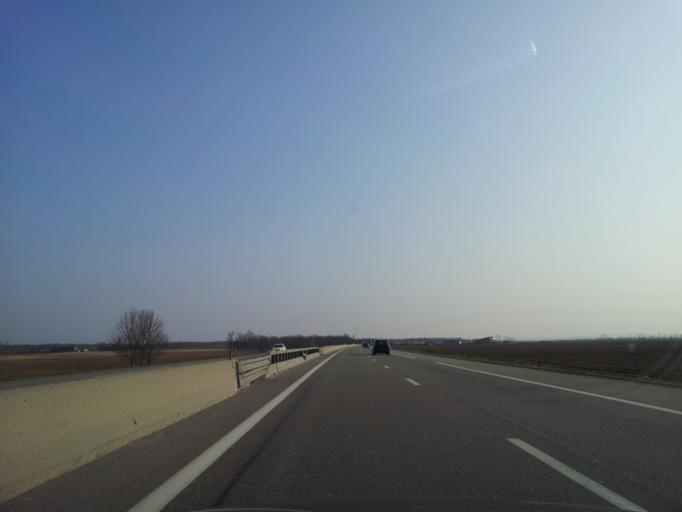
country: FR
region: Alsace
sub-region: Departement du Haut-Rhin
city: Ensisheim
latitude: 47.8678
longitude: 7.3902
